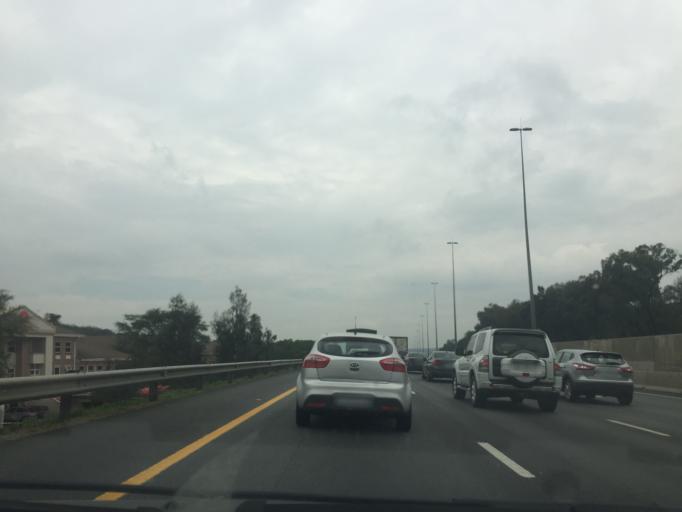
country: ZA
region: Gauteng
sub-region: City of Johannesburg Metropolitan Municipality
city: Midrand
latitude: -26.0340
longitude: 28.0357
